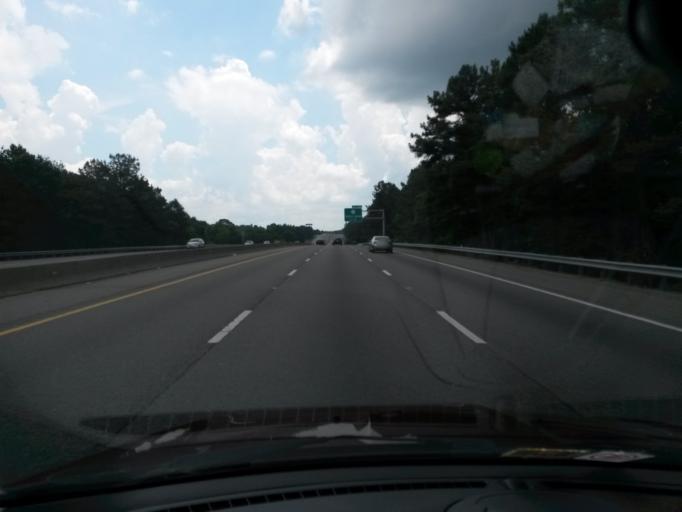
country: US
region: Virginia
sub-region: Chesterfield County
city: Bellwood
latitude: 37.4118
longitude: -77.4266
